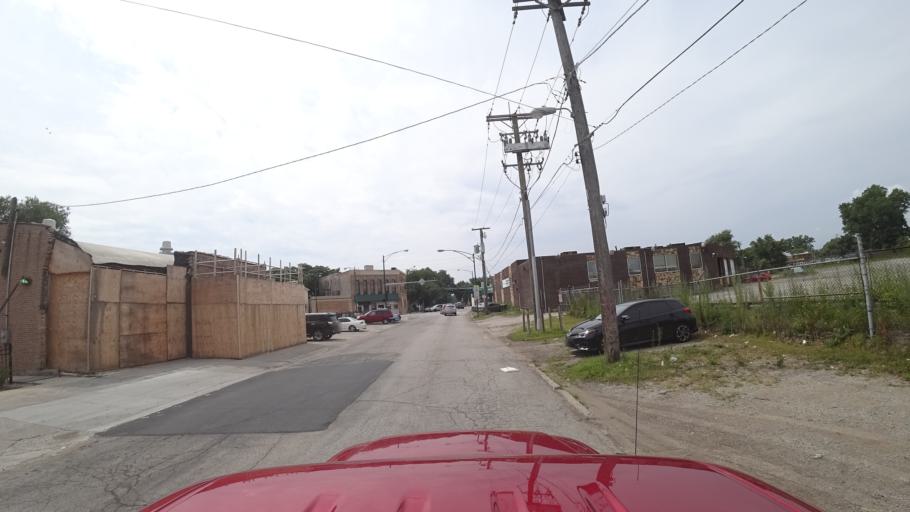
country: US
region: Illinois
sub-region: Cook County
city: Chicago
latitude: 41.8355
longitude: -87.6706
